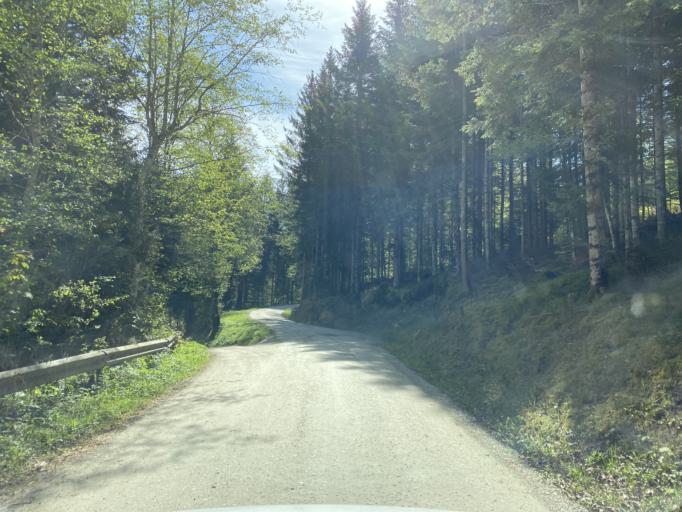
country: AT
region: Styria
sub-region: Politischer Bezirk Weiz
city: Birkfeld
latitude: 47.3428
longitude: 15.7065
